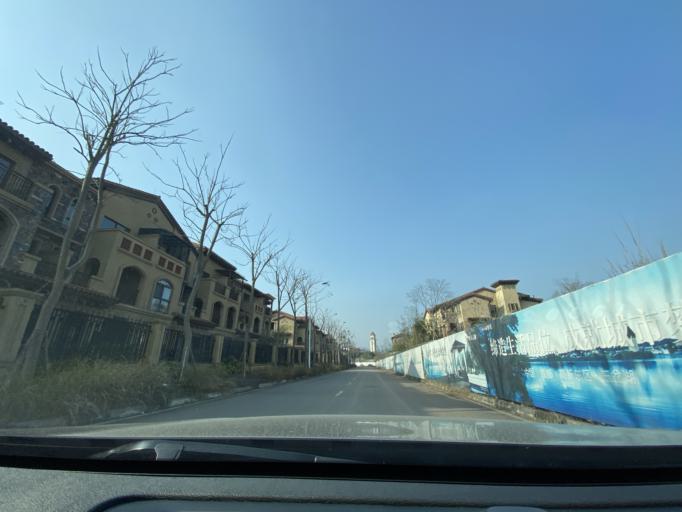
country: CN
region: Sichuan
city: Wenlin
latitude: 30.2533
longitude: 104.2457
